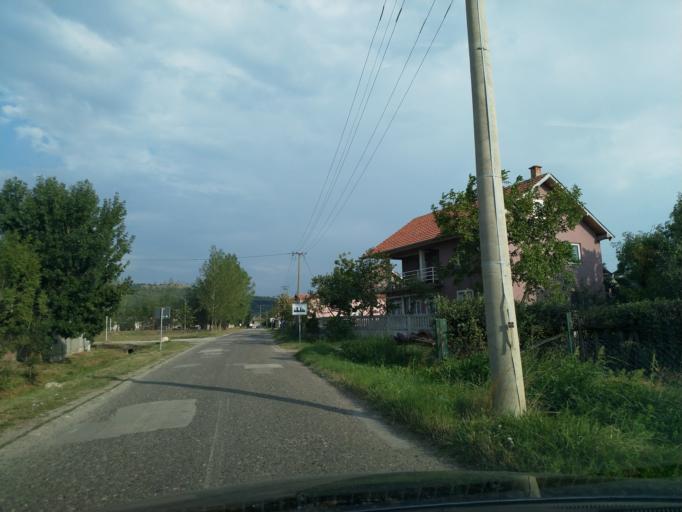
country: RS
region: Central Serbia
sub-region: Pomoravski Okrug
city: Paracin
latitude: 43.8222
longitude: 21.5382
